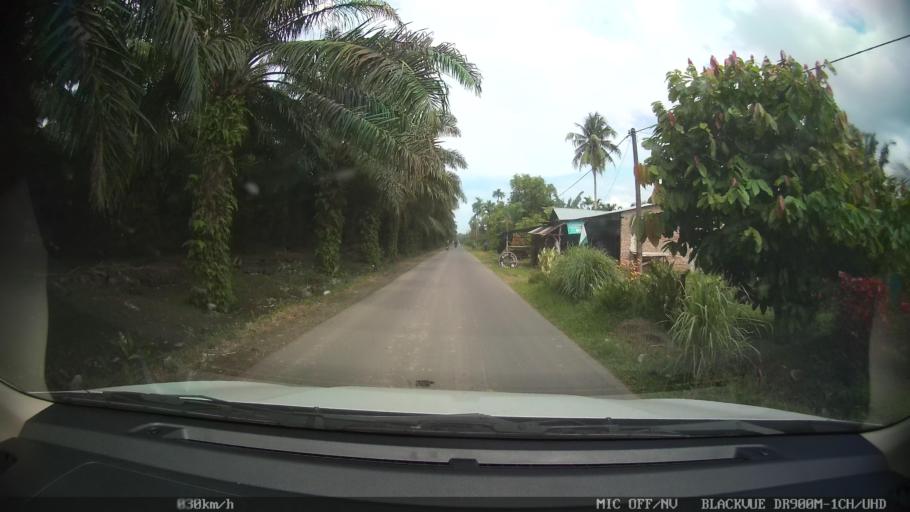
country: ID
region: North Sumatra
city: Sunggal
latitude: 3.6356
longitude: 98.6030
